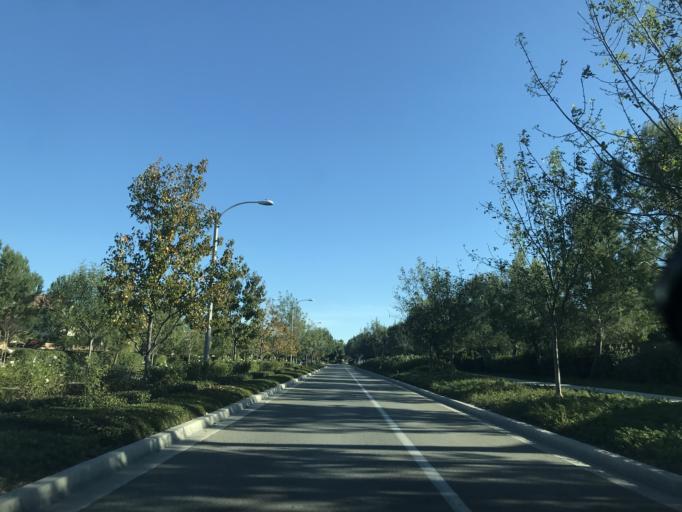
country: US
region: California
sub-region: Orange County
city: Lake Forest
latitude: 33.7043
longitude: -117.7397
